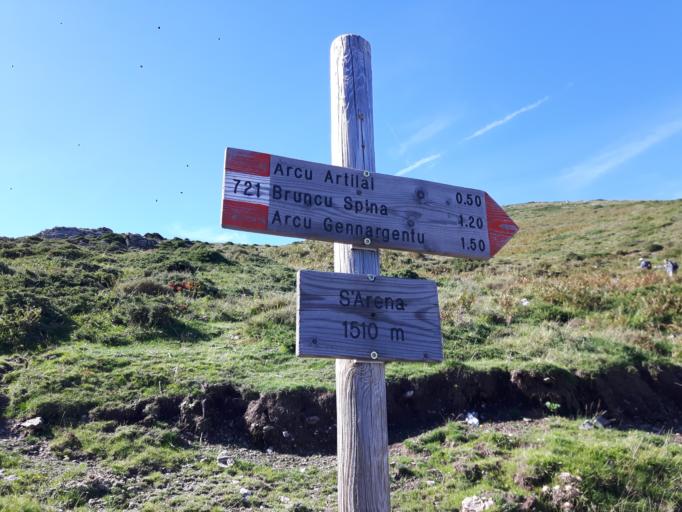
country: IT
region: Sardinia
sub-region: Provincia di Nuoro
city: Desulo
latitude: 40.0191
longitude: 9.2781
